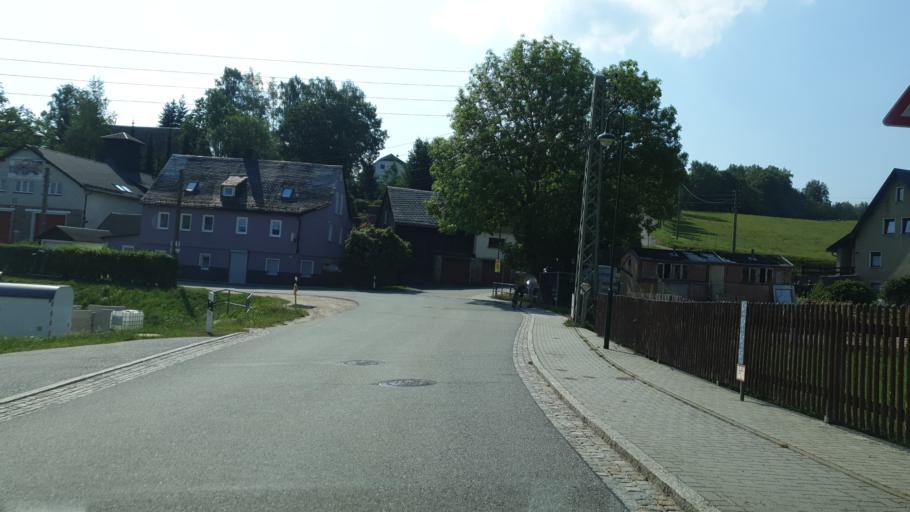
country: DE
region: Saxony
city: Zschorlau
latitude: 50.5483
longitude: 12.6548
